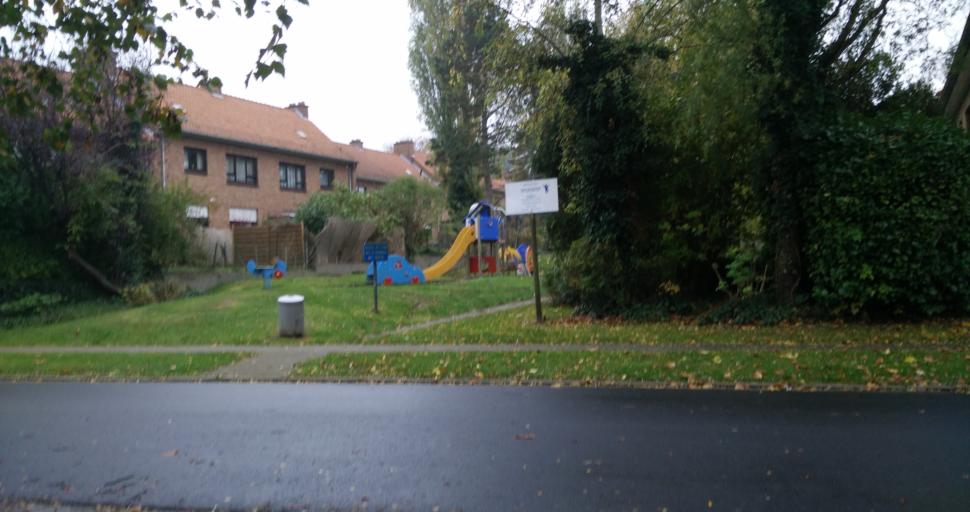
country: BE
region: Flanders
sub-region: Provincie Vlaams-Brabant
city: Halle
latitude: 50.7279
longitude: 4.2499
